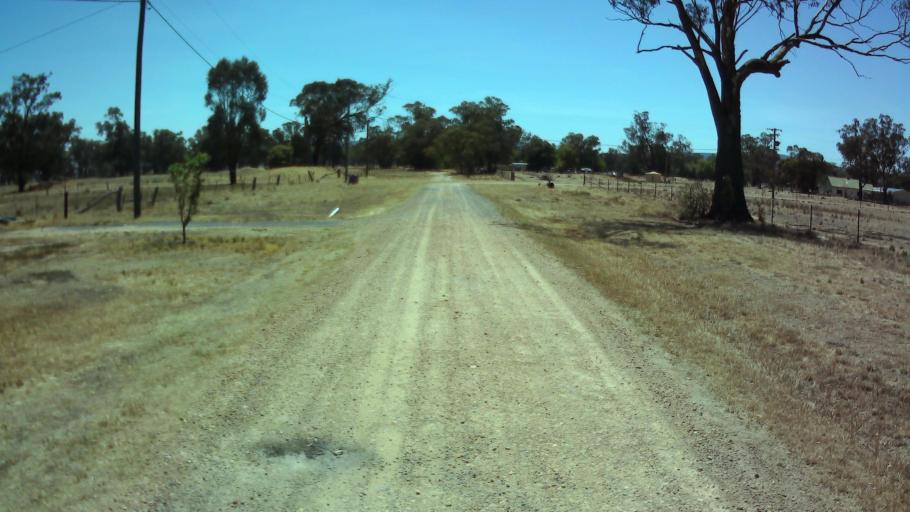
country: AU
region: New South Wales
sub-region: Weddin
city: Grenfell
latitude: -34.0378
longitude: 147.9268
